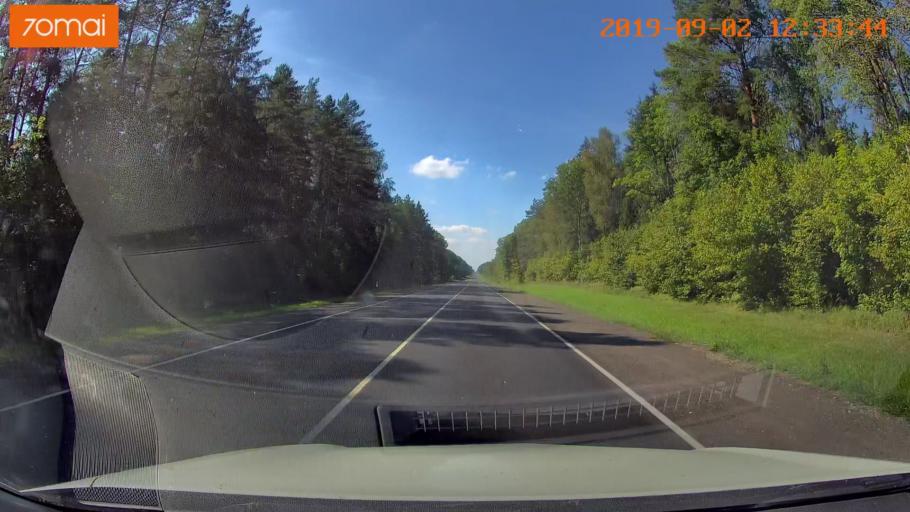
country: RU
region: Smolensk
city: Shumyachi
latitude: 53.8155
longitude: 32.4212
